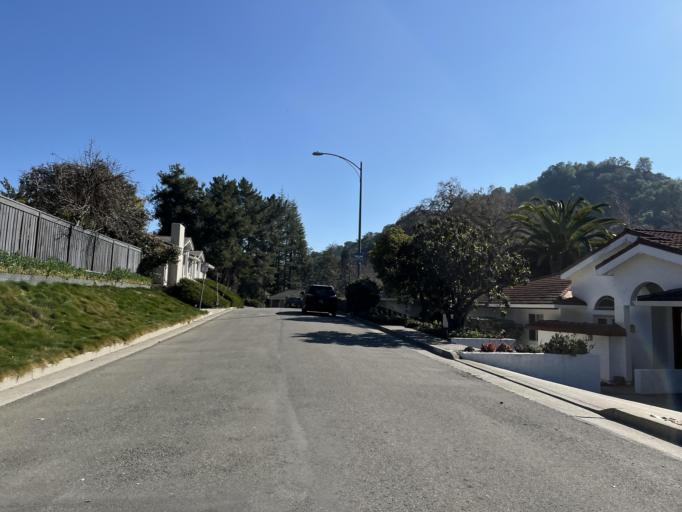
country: US
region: California
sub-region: Santa Clara County
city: Cupertino
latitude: 37.3098
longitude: -122.0660
